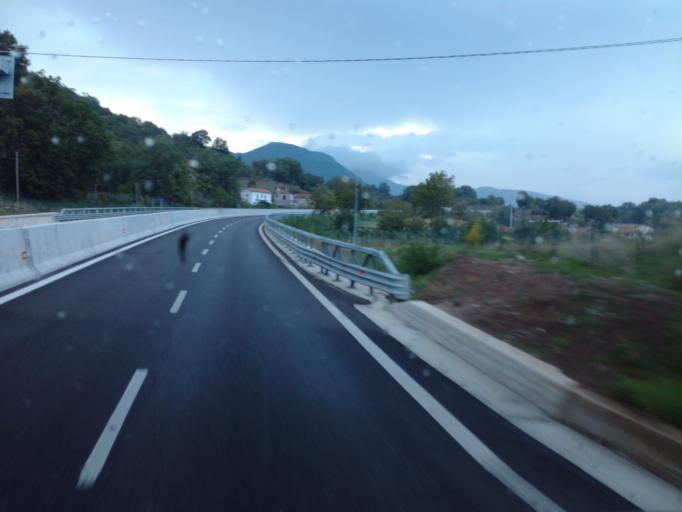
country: IT
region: Calabria
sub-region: Provincia di Cosenza
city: Laino Borgo
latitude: 39.9678
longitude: 15.9326
